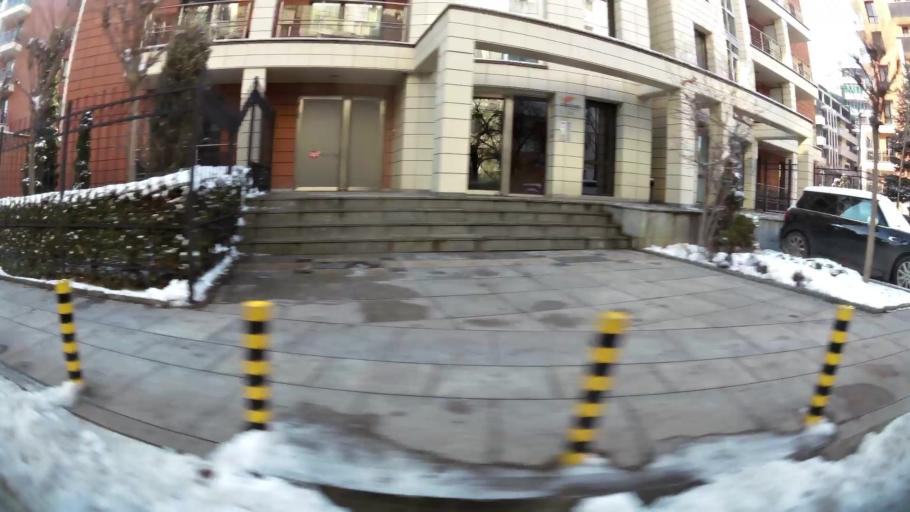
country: BG
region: Sofia-Capital
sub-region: Stolichna Obshtina
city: Sofia
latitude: 42.6700
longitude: 23.3540
